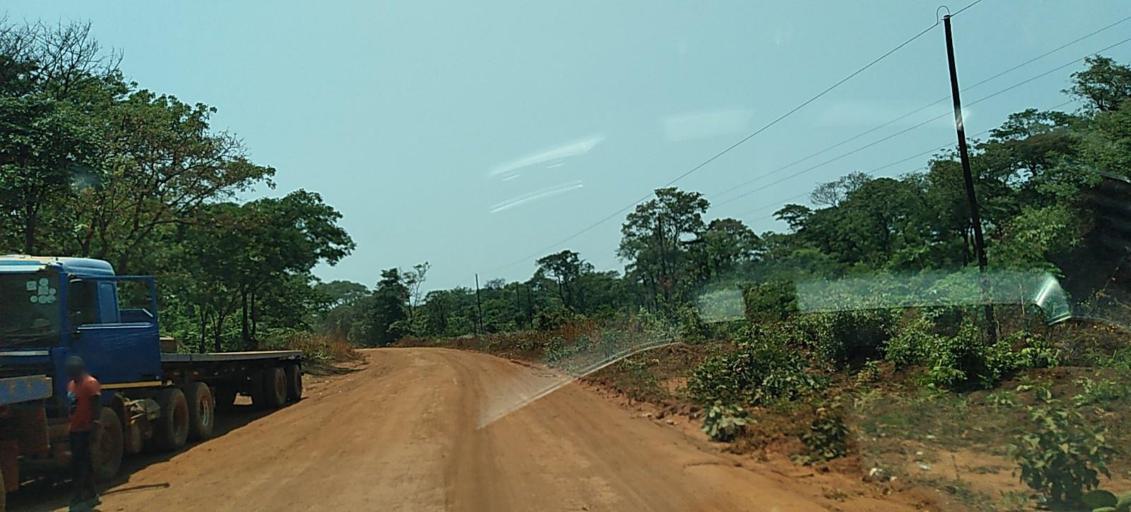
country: ZM
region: North-Western
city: Kansanshi
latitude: -11.9907
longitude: 26.8369
